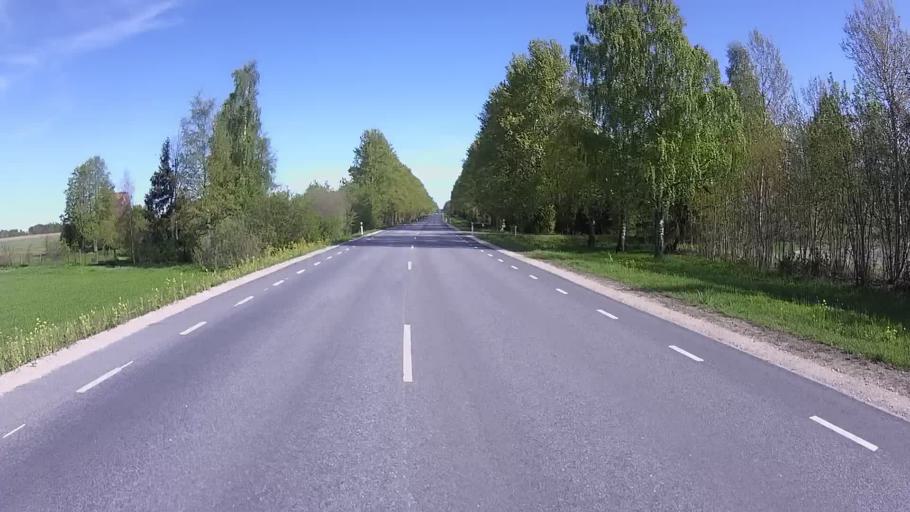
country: EE
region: Polvamaa
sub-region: Polva linn
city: Polva
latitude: 58.2733
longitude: 27.0029
